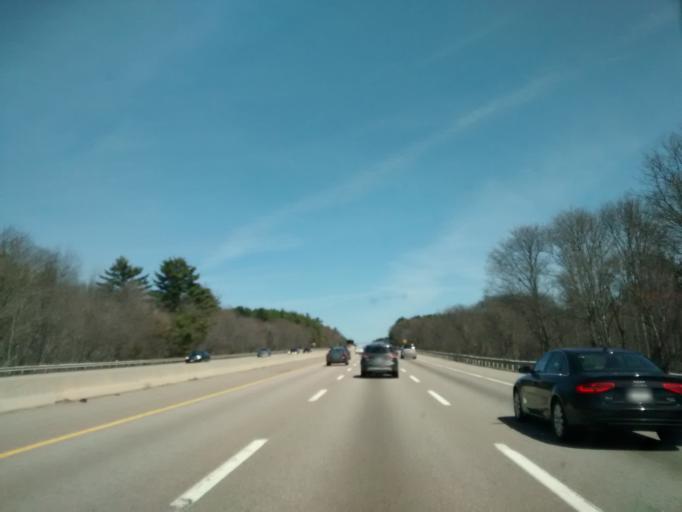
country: US
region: Massachusetts
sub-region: Worcester County
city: Cordaville
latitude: 42.2772
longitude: -71.5282
